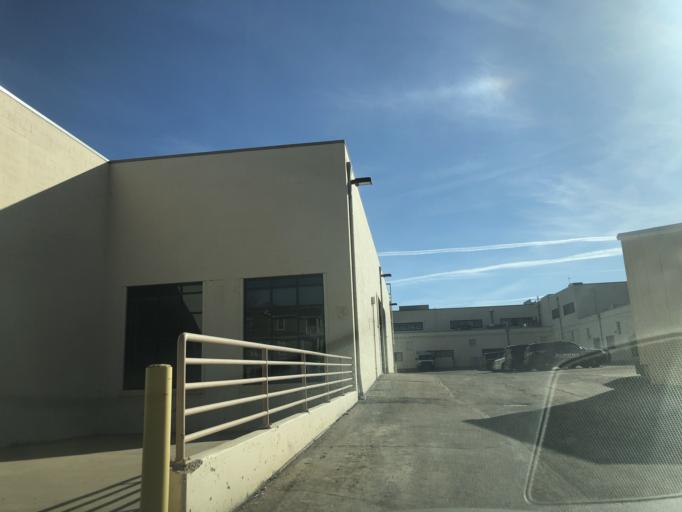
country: US
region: Colorado
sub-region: Adams County
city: Aurora
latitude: 39.7201
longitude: -104.8062
